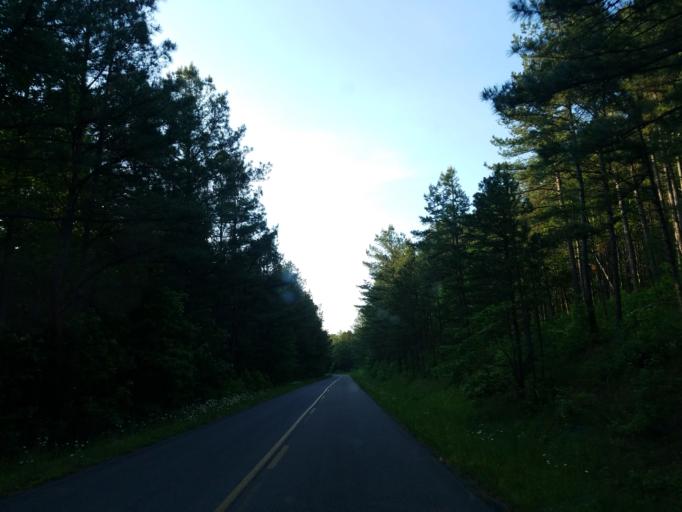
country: US
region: Georgia
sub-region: Whitfield County
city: Dalton
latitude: 34.6385
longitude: -85.0834
